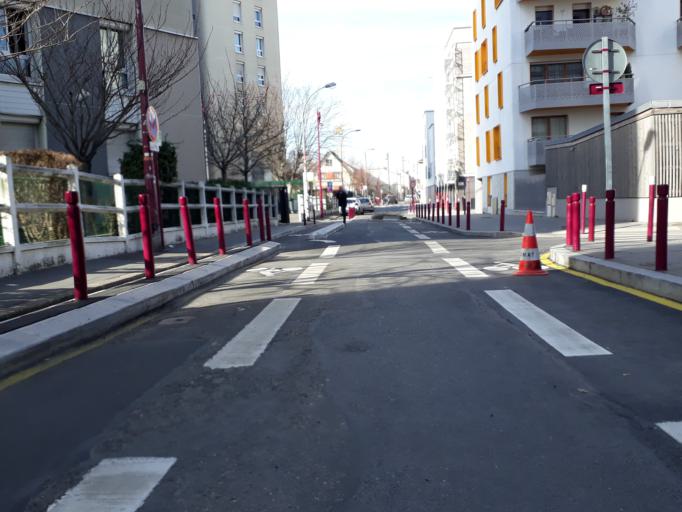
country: FR
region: Ile-de-France
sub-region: Departement du Val-d'Oise
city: Bezons
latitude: 48.9233
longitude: 2.2163
